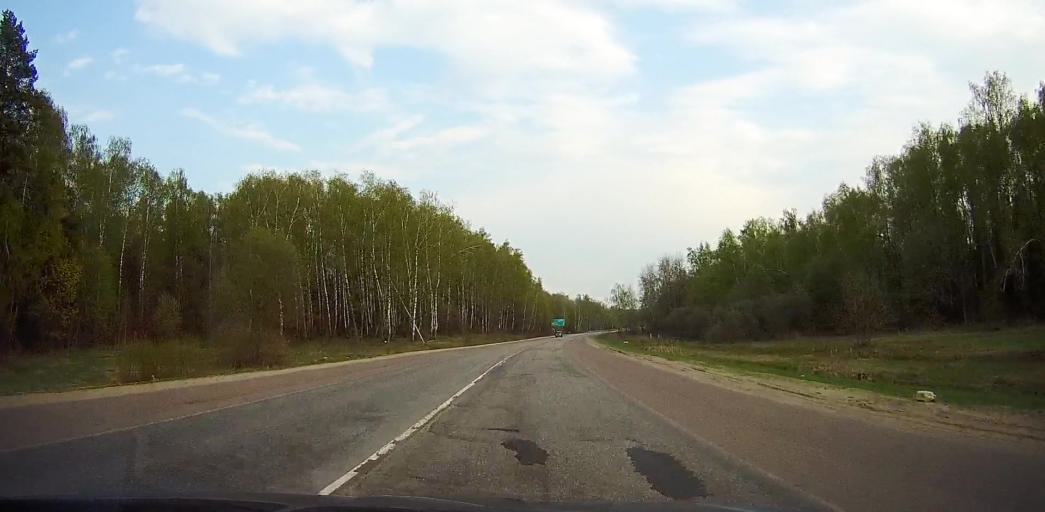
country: RU
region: Moskovskaya
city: Petrovskaya
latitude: 55.5300
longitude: 37.7827
